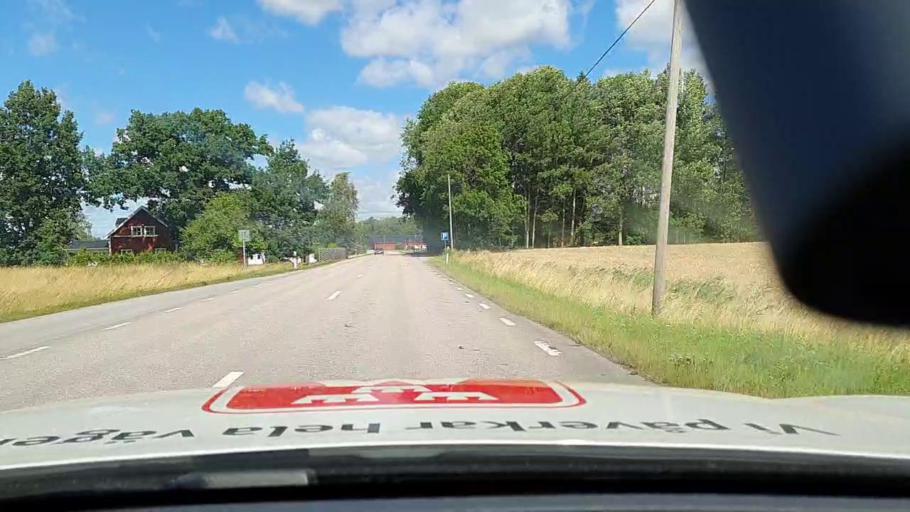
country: SE
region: Vaestra Goetaland
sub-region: Skovde Kommun
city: Stopen
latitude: 58.5136
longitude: 13.9745
